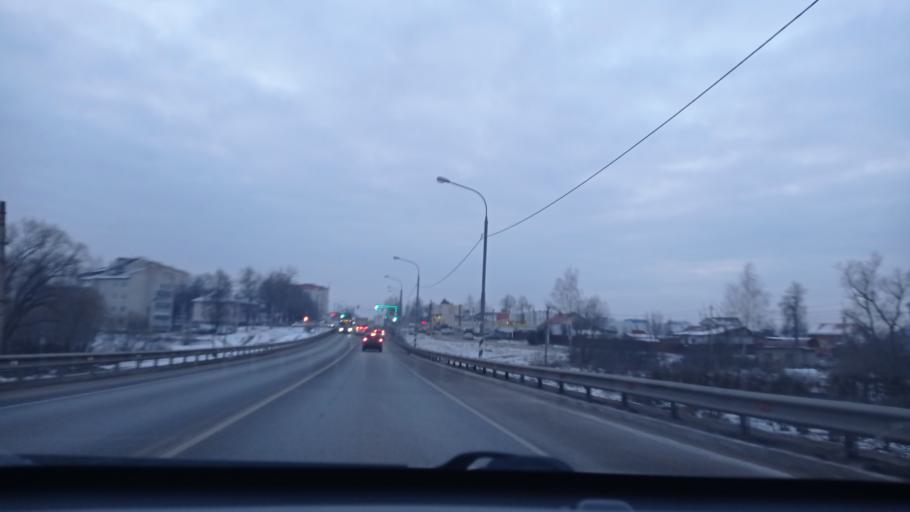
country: RU
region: Kaluga
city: Belousovo
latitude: 55.0935
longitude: 36.6678
